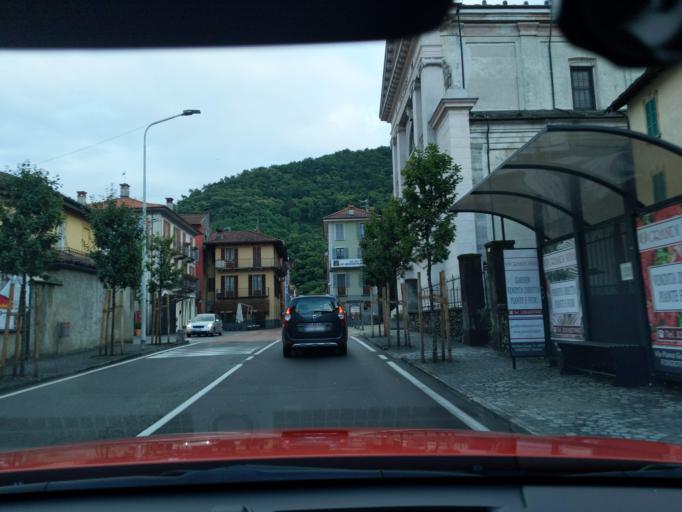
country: IT
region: Piedmont
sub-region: Provincia Verbano-Cusio-Ossola
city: Cannobio
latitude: 46.0621
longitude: 8.6977
